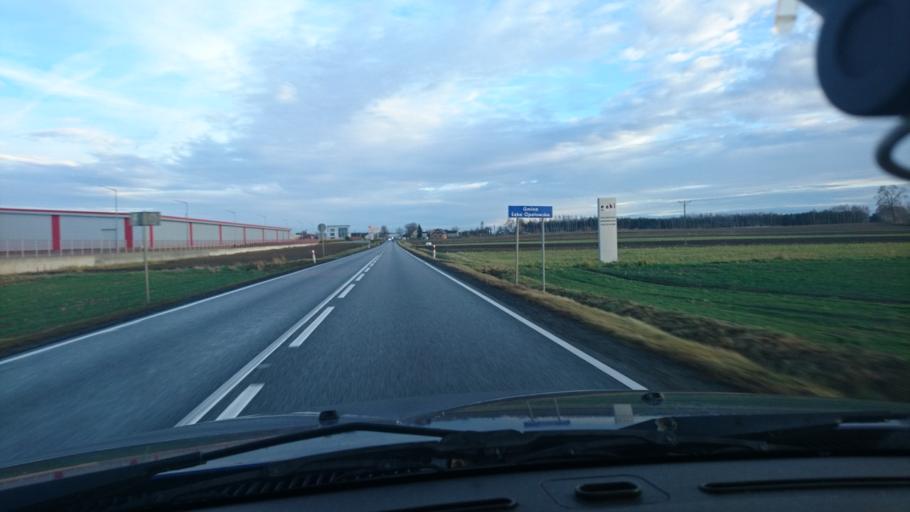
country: PL
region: Greater Poland Voivodeship
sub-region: Powiat kepinski
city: Slupia pod Kepnem
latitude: 51.2322
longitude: 18.0673
